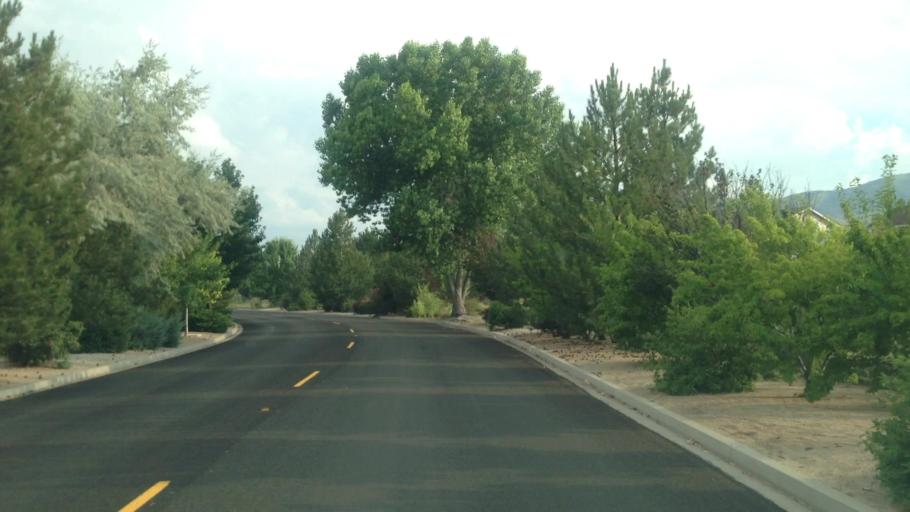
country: US
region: Nevada
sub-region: Washoe County
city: Lemmon Valley
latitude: 39.6306
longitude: -119.8755
